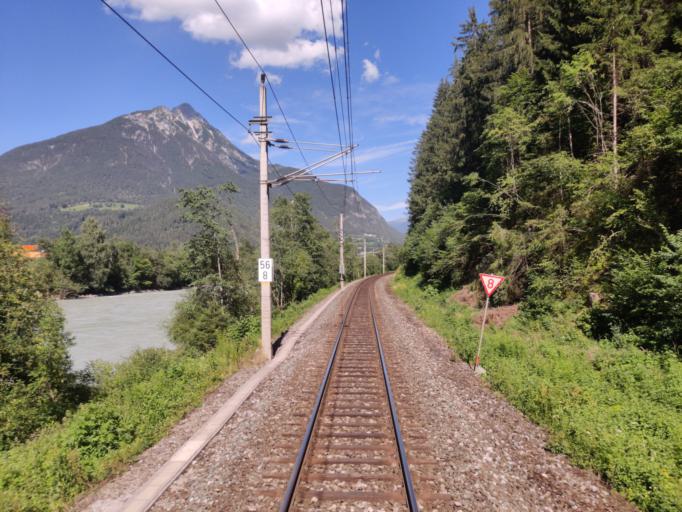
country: AT
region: Tyrol
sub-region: Politischer Bezirk Imst
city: Imst
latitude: 47.2156
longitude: 10.7347
